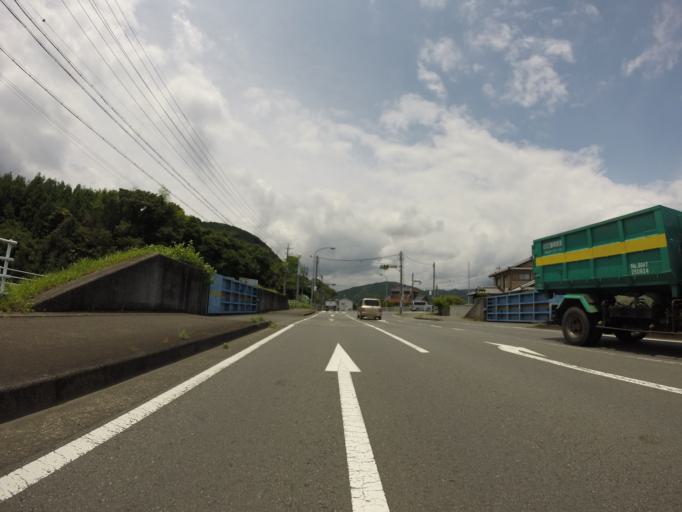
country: JP
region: Shizuoka
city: Shizuoka-shi
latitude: 34.9751
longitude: 138.3410
